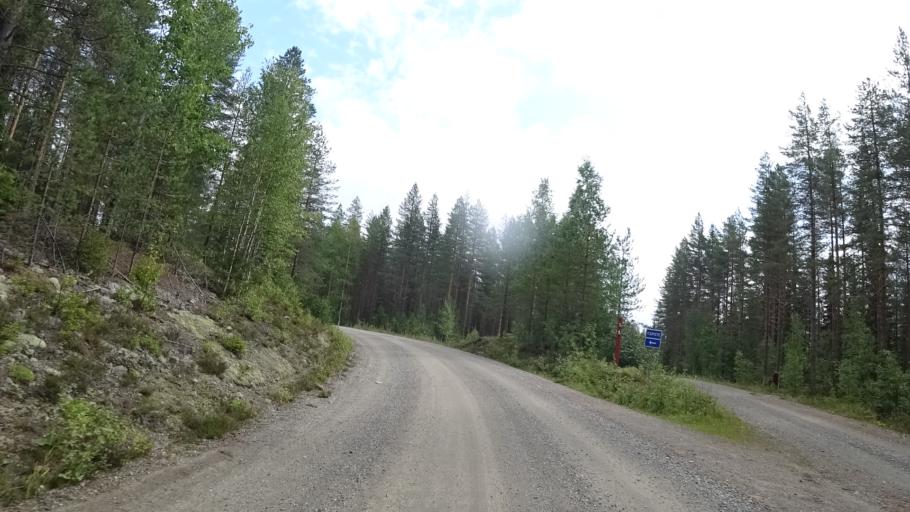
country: FI
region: North Karelia
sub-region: Joensuu
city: Ilomantsi
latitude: 62.9206
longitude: 31.3427
